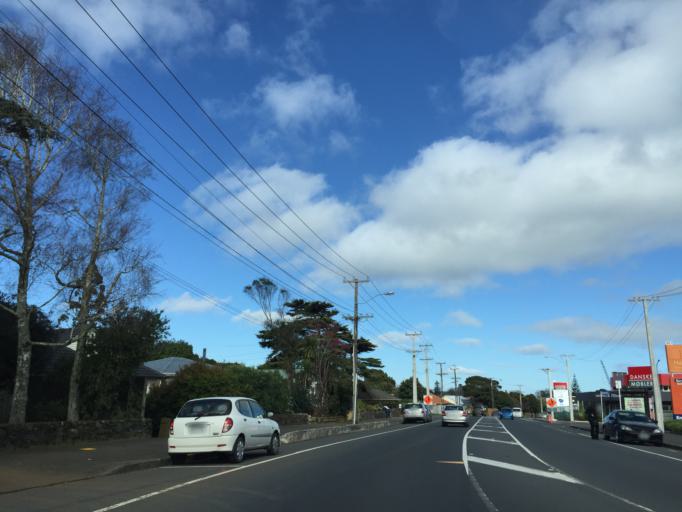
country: NZ
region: Auckland
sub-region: Auckland
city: Auckland
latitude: -36.9019
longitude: 174.7593
